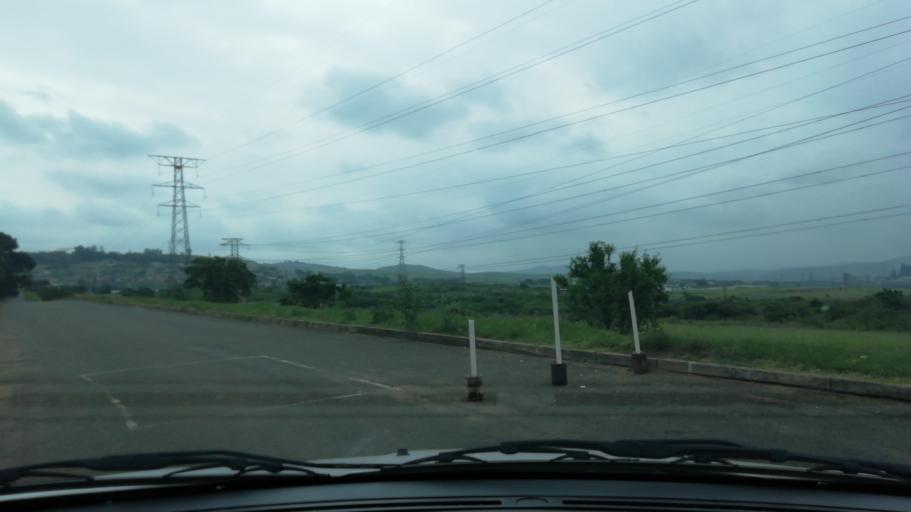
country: ZA
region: KwaZulu-Natal
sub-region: uThungulu District Municipality
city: Empangeni
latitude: -28.7365
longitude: 31.8909
